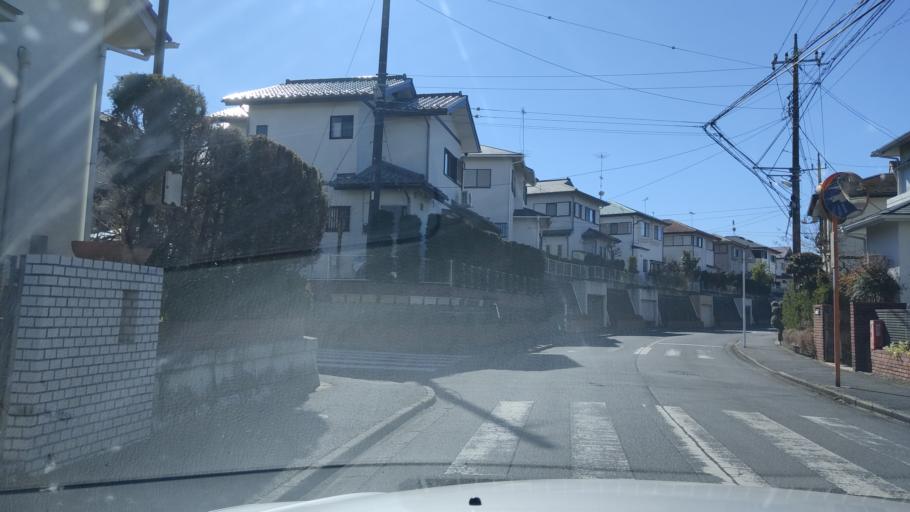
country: JP
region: Chiba
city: Nagareyama
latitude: 35.9072
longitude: 139.9168
